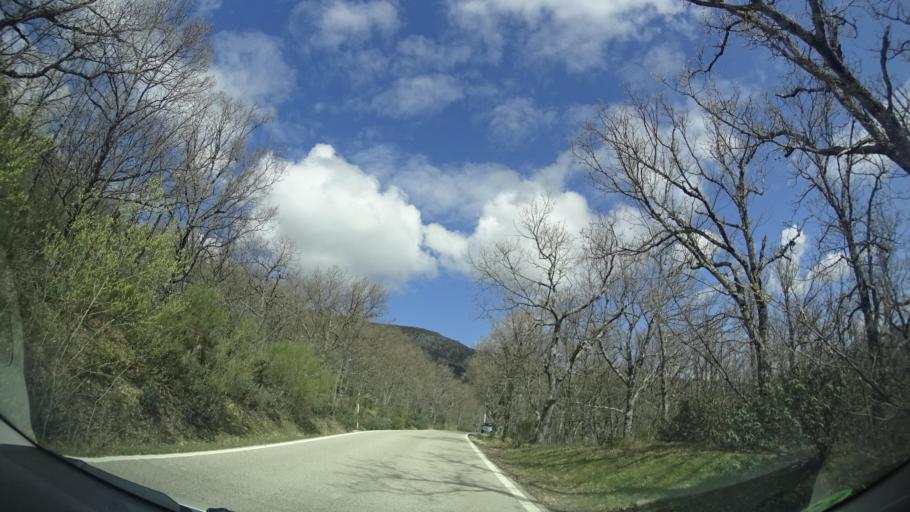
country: ES
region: Madrid
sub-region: Provincia de Madrid
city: Miraflores de la Sierra
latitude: 40.8294
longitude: -3.7663
